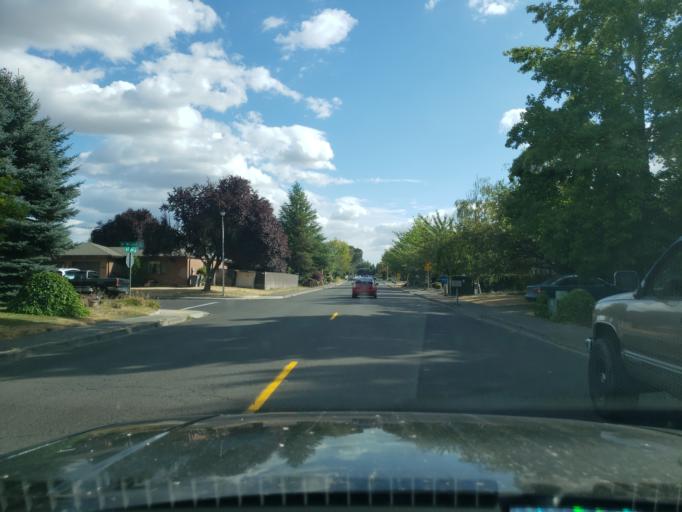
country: US
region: Oregon
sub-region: Yamhill County
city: McMinnville
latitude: 45.2058
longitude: -123.2196
